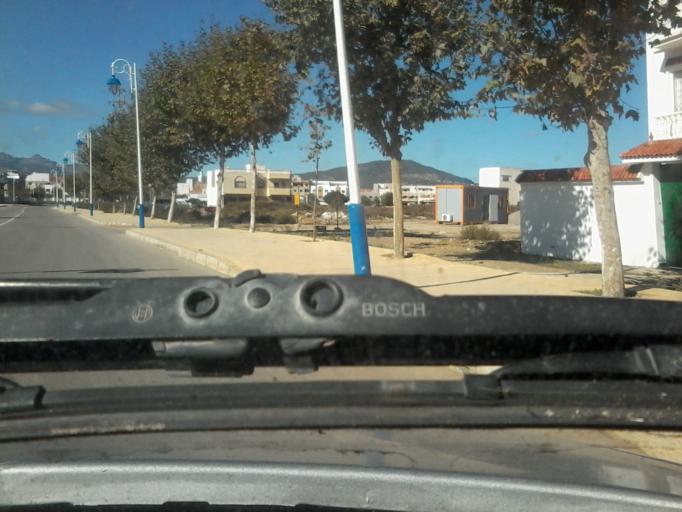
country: MA
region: Tanger-Tetouan
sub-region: Tetouan
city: Martil
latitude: 35.6944
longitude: -5.3426
